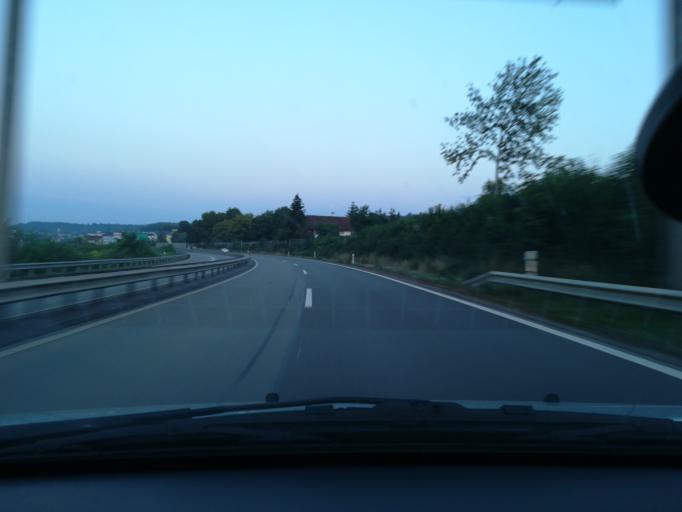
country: CH
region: Schaffhausen
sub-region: Bezirk Reiat
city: Stetten
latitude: 47.7189
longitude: 8.6584
